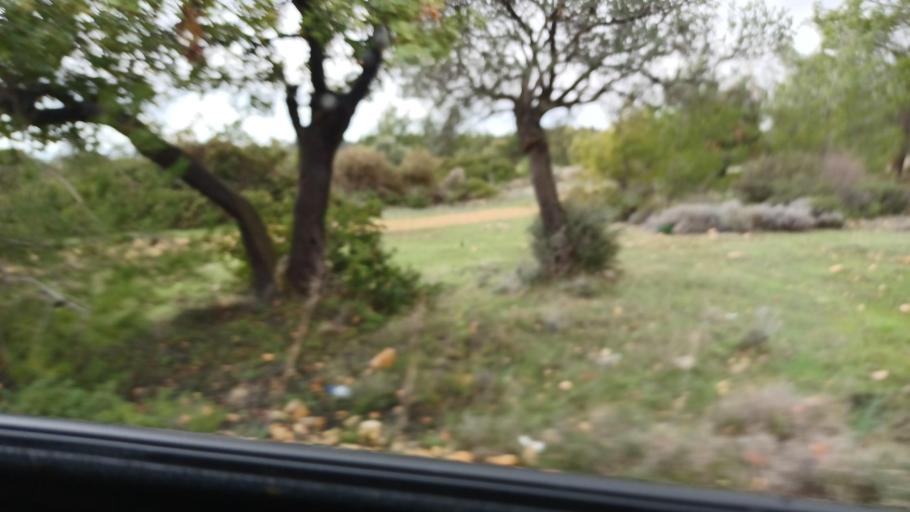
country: CY
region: Limassol
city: Sotira
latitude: 34.7386
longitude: 32.8612
